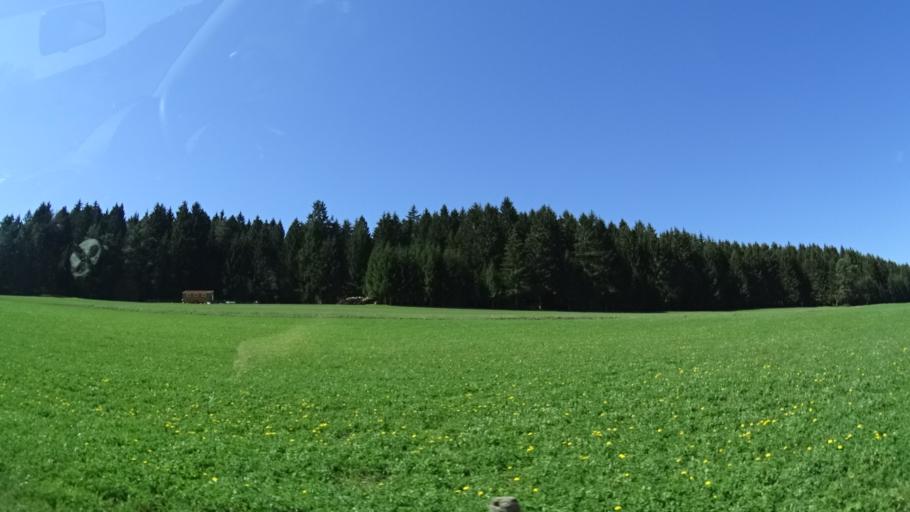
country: DE
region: Bavaria
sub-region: Upper Palatinate
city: Lauterhofen
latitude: 49.4105
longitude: 11.6217
